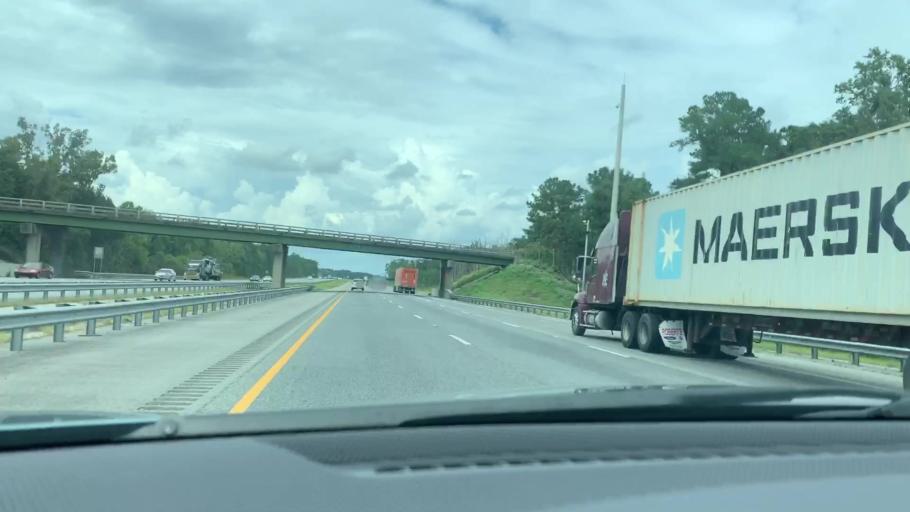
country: US
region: Georgia
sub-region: McIntosh County
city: Darien
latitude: 31.4640
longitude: -81.4463
